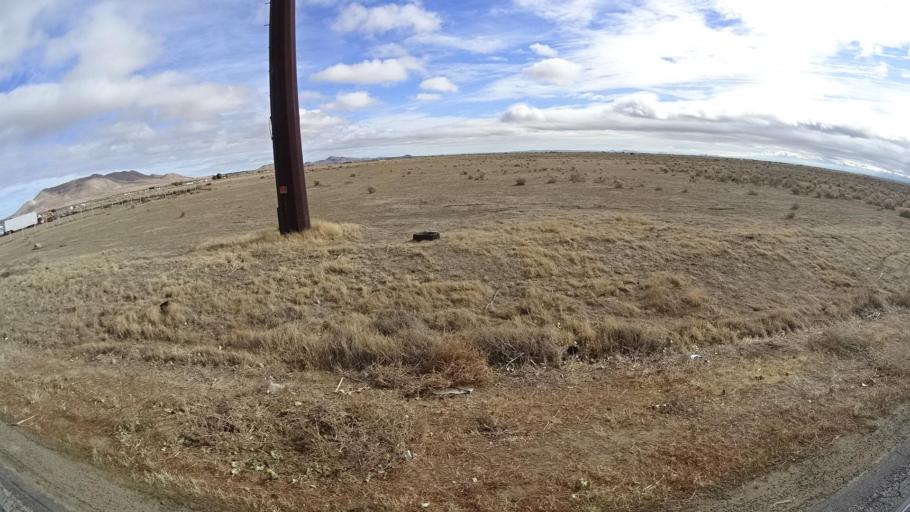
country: US
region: California
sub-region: Kern County
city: Rosamond
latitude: 34.8540
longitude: -118.3089
